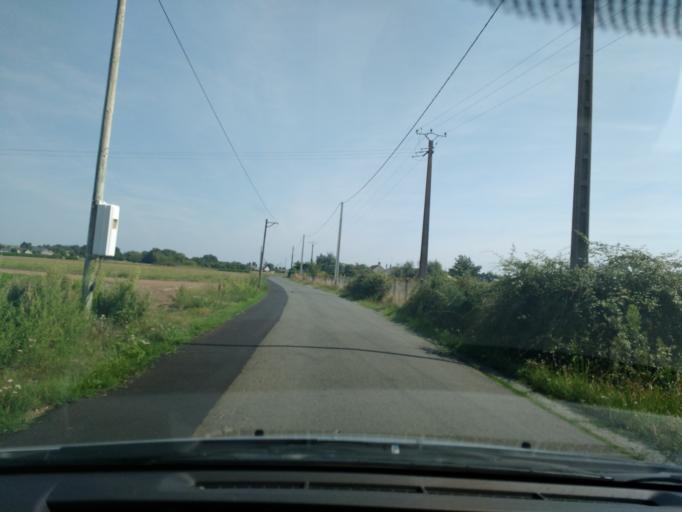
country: FR
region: Pays de la Loire
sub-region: Departement de Maine-et-Loire
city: Maze
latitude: 47.4661
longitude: -0.2925
